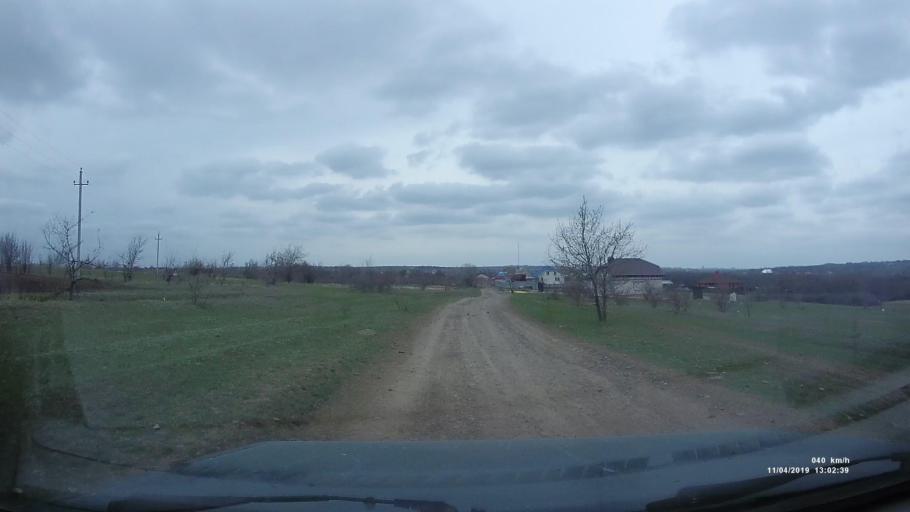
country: RU
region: Rostov
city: Staraya Stanitsa
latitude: 48.2879
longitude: 40.3563
